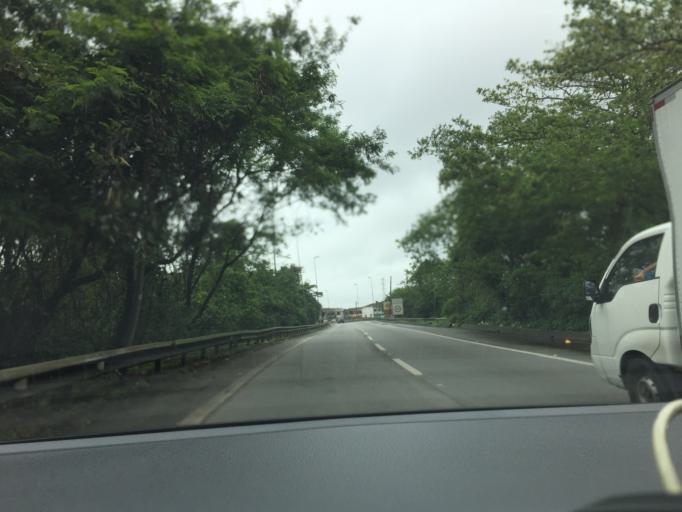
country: BR
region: Sao Paulo
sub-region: Guaruja
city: Guaruja
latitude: -23.9676
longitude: -46.2716
